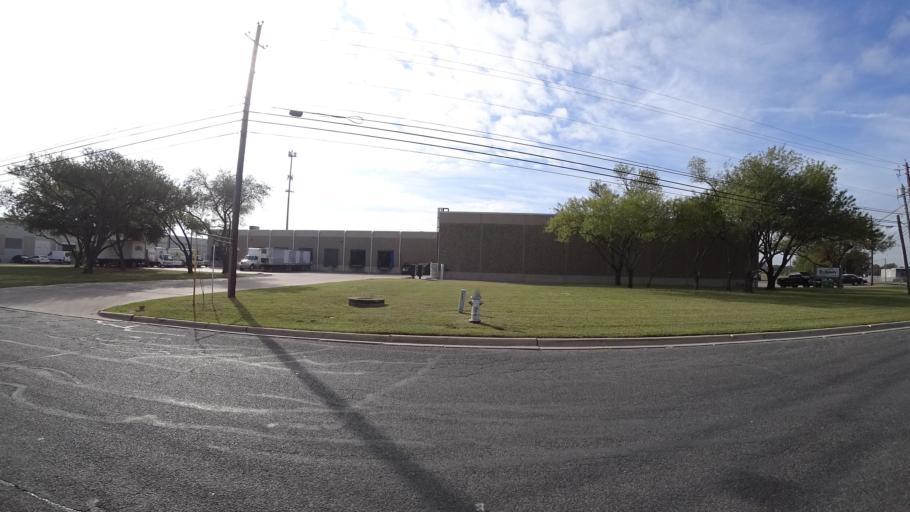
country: US
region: Texas
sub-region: Travis County
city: Austin
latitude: 30.2110
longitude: -97.7332
